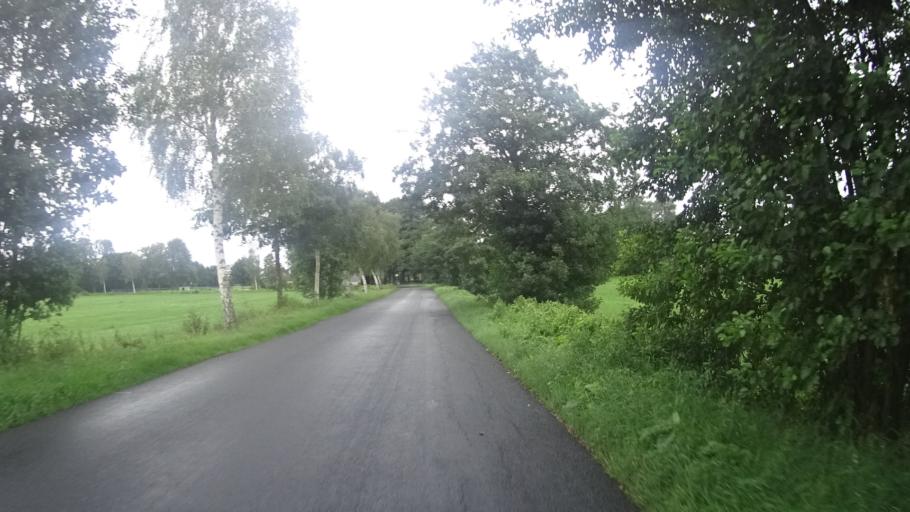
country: DE
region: Schleswig-Holstein
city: Raa-Besenbek
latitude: 53.7882
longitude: 9.5946
